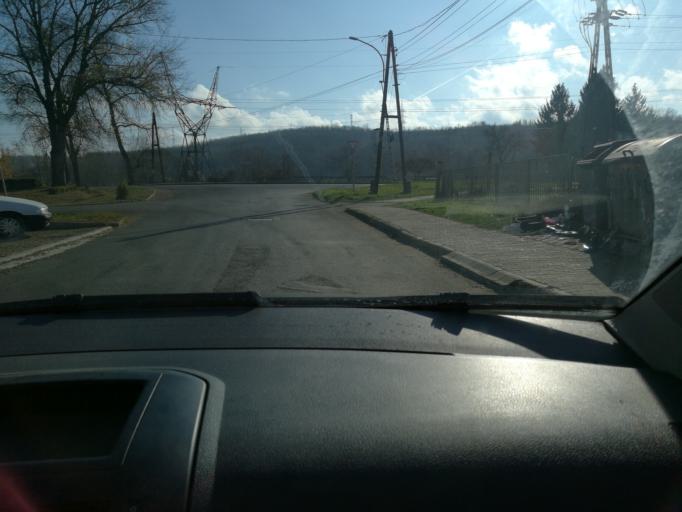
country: HU
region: Nograd
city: Batonyterenye
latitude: 47.9853
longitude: 19.8254
